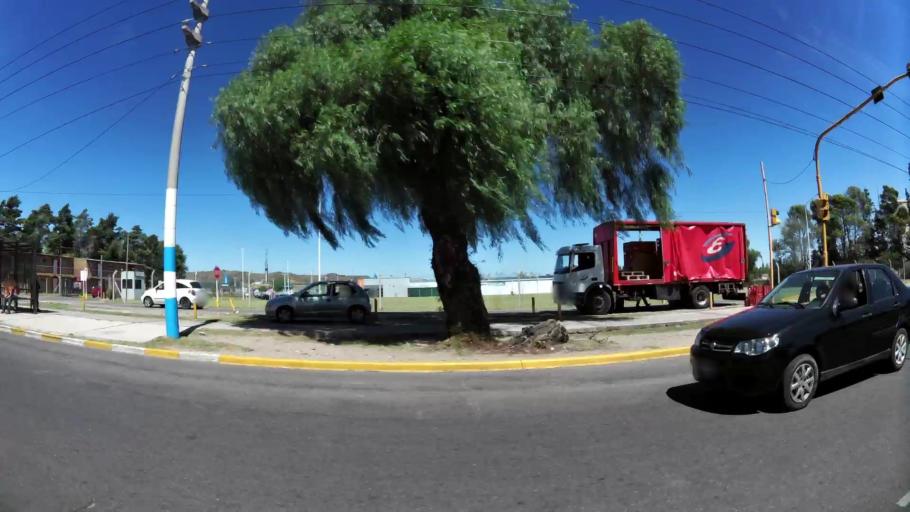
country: AR
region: San Luis
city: San Luis
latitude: -33.2943
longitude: -66.3031
